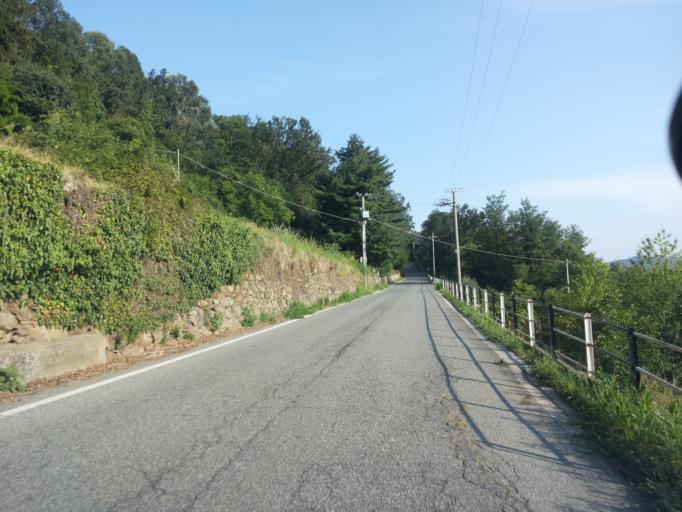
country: IT
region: Piedmont
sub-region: Provincia di Biella
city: Magnano
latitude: 45.4555
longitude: 7.9944
